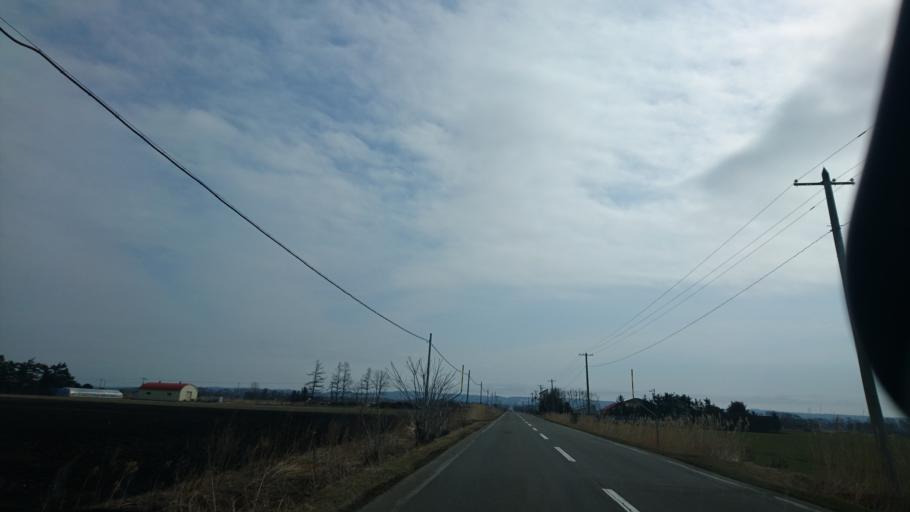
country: JP
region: Hokkaido
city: Otofuke
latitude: 43.0392
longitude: 143.2249
